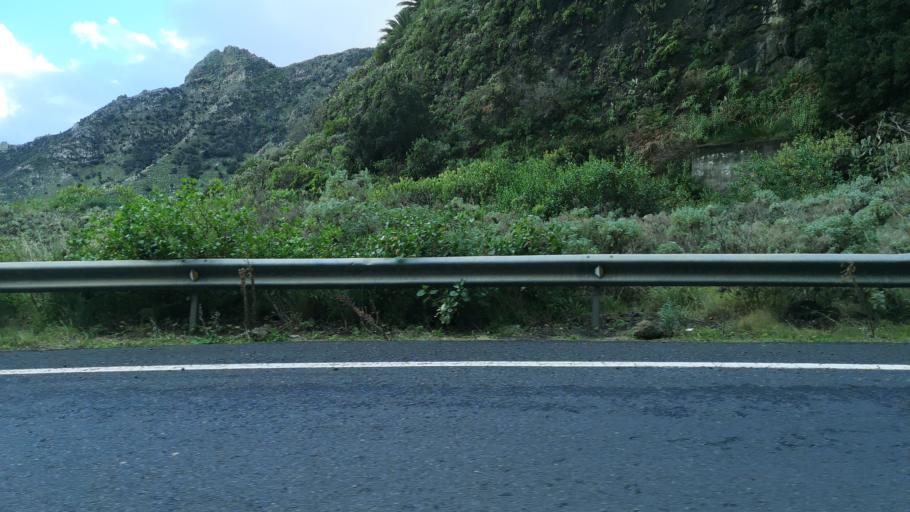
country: ES
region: Canary Islands
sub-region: Provincia de Santa Cruz de Tenerife
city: Hermigua
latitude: 28.1310
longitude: -17.1858
